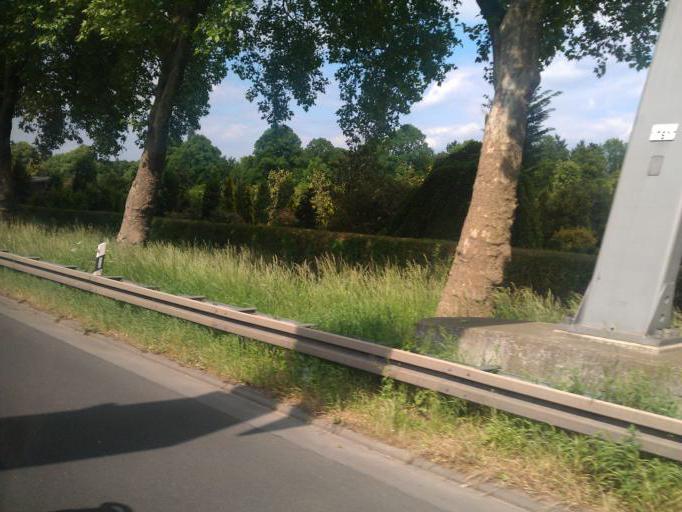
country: DE
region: North Rhine-Westphalia
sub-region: Regierungsbezirk Koln
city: Bayenthal
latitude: 50.8744
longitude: 6.9697
